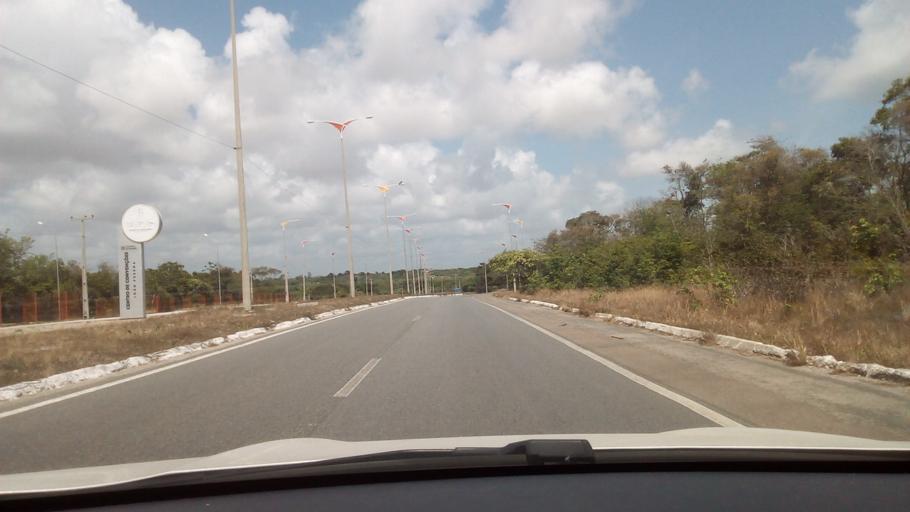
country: BR
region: Paraiba
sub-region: Joao Pessoa
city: Joao Pessoa
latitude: -7.1855
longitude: -34.8028
